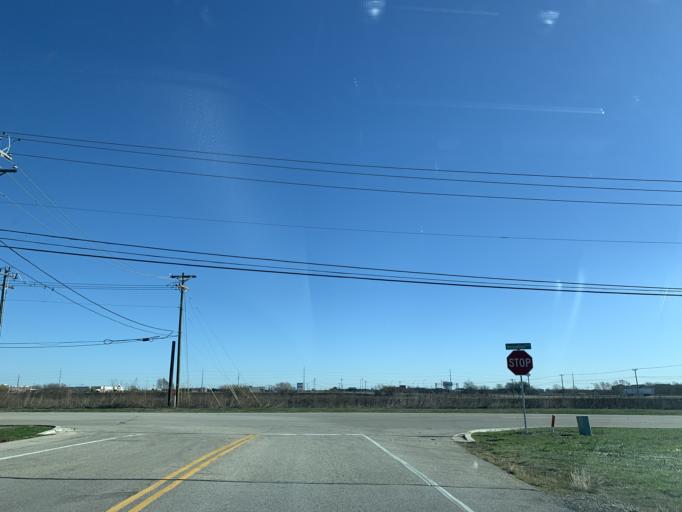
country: US
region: Texas
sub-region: Williamson County
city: Hutto
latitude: 30.5406
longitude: -97.5745
